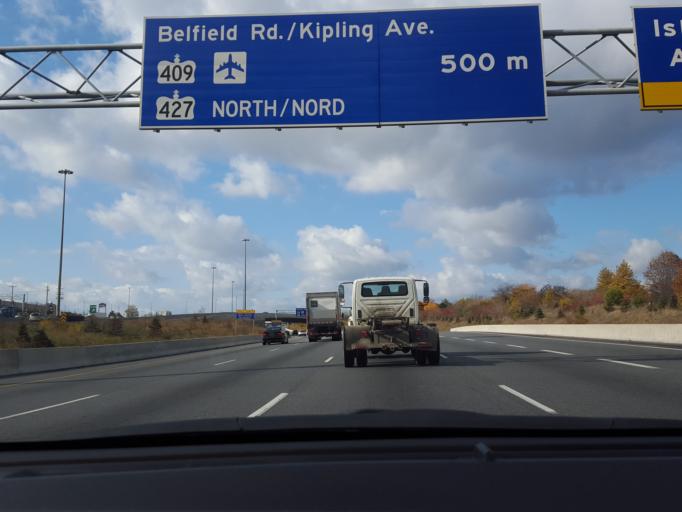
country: CA
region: Ontario
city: Etobicoke
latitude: 43.7120
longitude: -79.5438
